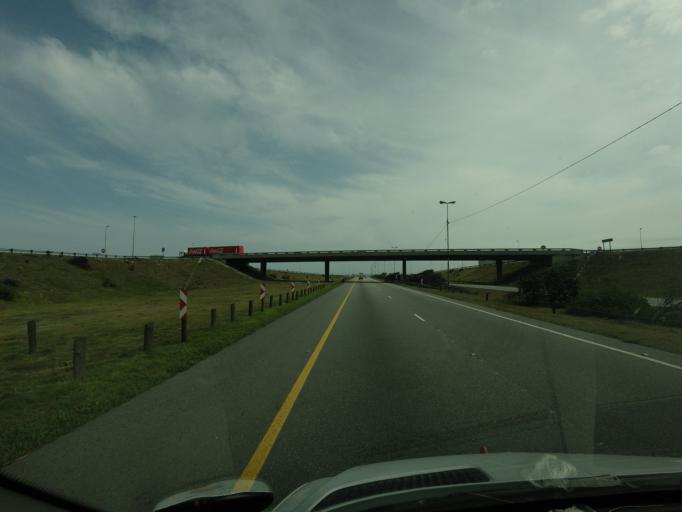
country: ZA
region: Eastern Cape
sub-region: Nelson Mandela Bay Metropolitan Municipality
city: Port Elizabeth
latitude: -33.8822
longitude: 25.6235
